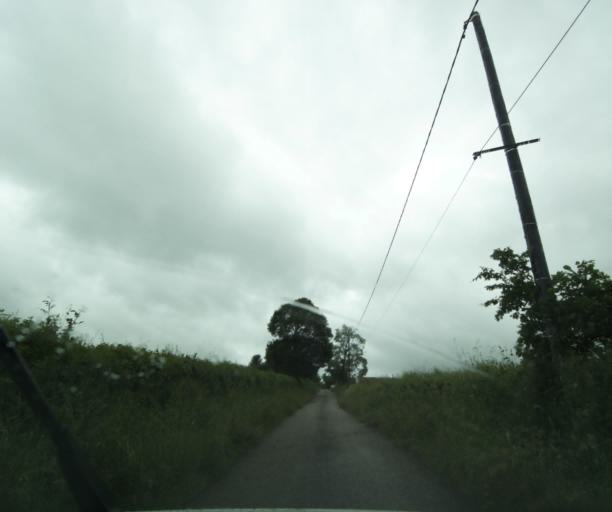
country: FR
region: Bourgogne
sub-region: Departement de Saone-et-Loire
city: Matour
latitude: 46.4580
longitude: 4.4692
